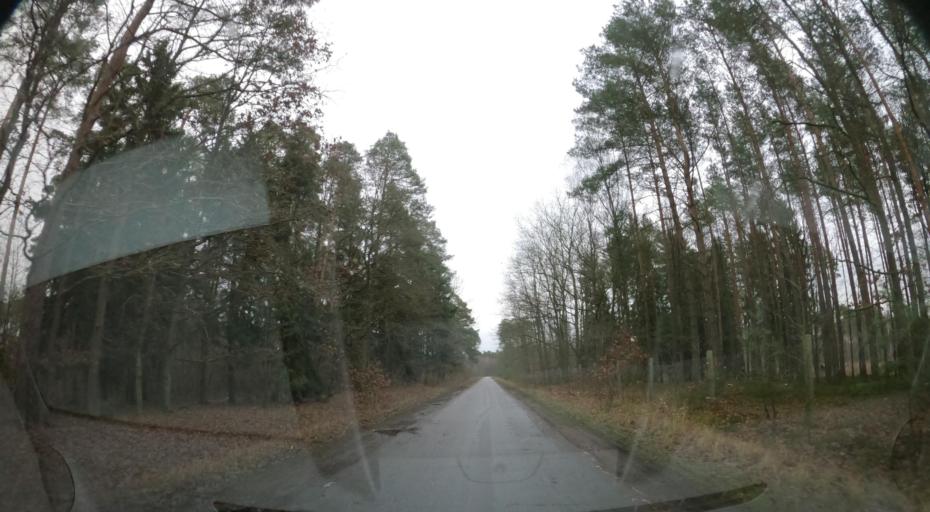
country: PL
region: Greater Poland Voivodeship
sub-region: Powiat zlotowski
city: Krajenka
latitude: 53.2881
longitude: 17.0533
